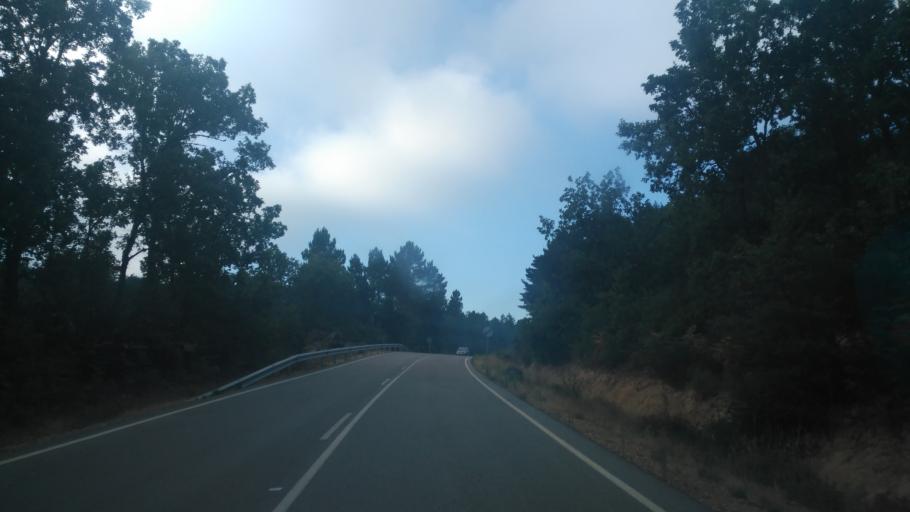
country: ES
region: Castille and Leon
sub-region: Provincia de Salamanca
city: Nava de Francia
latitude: 40.5370
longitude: -6.1370
